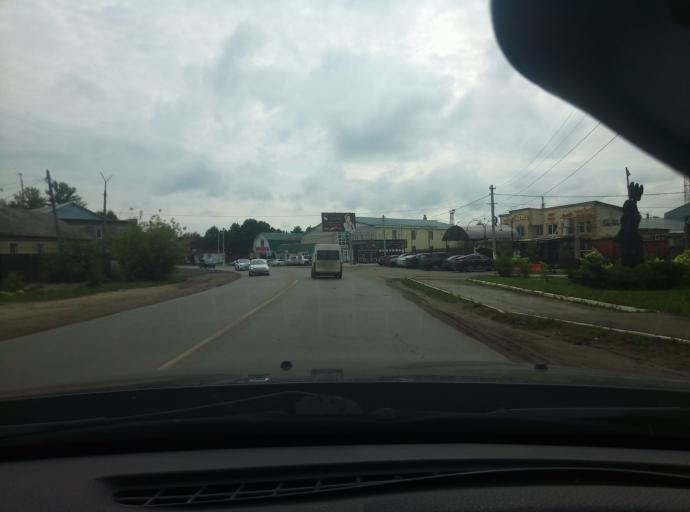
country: RU
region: Tula
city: Donskoy
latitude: 53.9683
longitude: 38.3467
